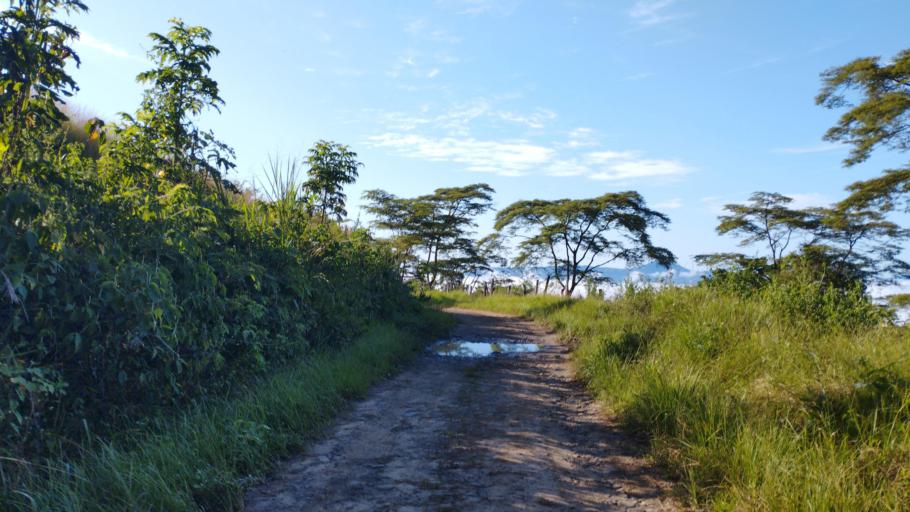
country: CO
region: Casanare
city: Sabanalarga
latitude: 4.7819
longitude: -73.0847
